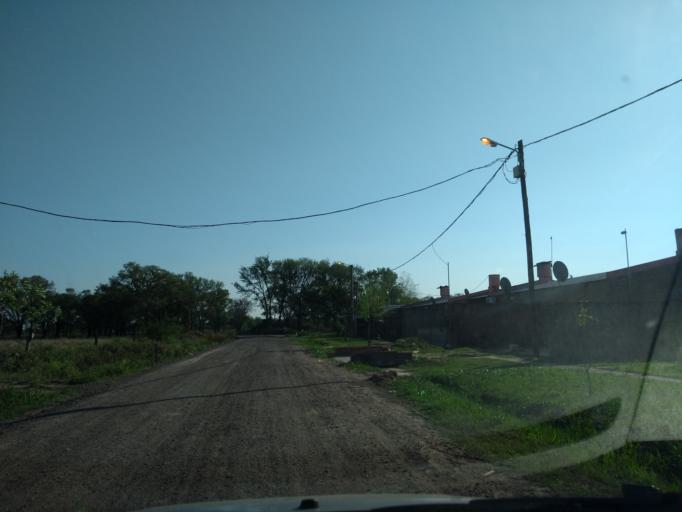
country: AR
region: Chaco
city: Fontana
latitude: -27.4164
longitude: -59.0530
